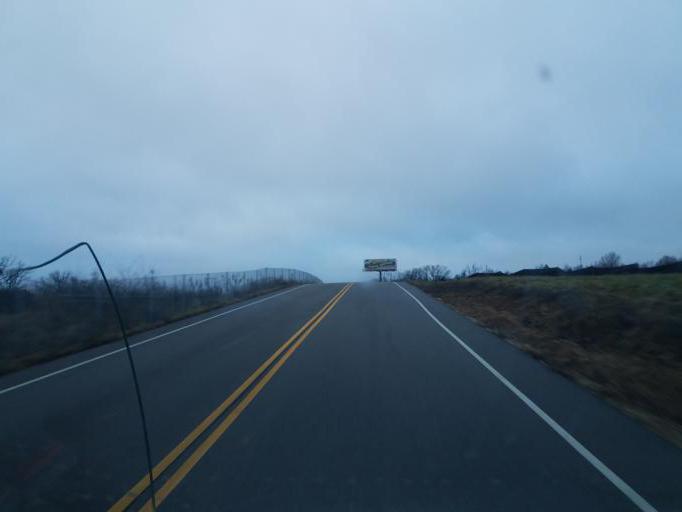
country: US
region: Missouri
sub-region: Phelps County
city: Rolla
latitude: 37.9762
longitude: -91.7387
